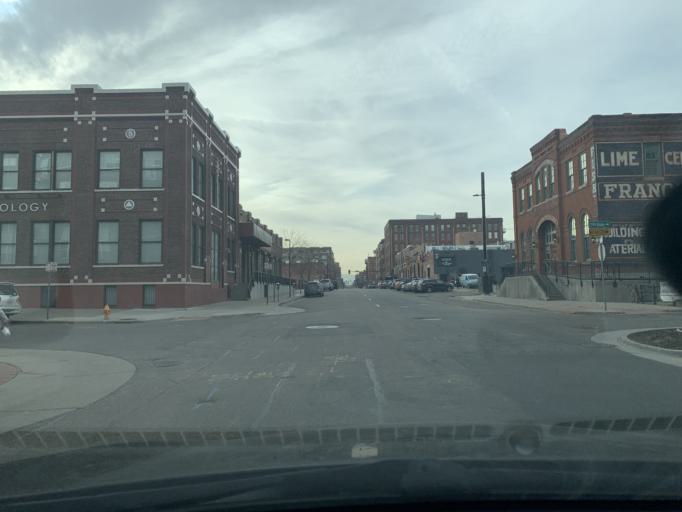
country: US
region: Colorado
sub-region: Denver County
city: Denver
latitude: 39.7581
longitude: -104.9894
